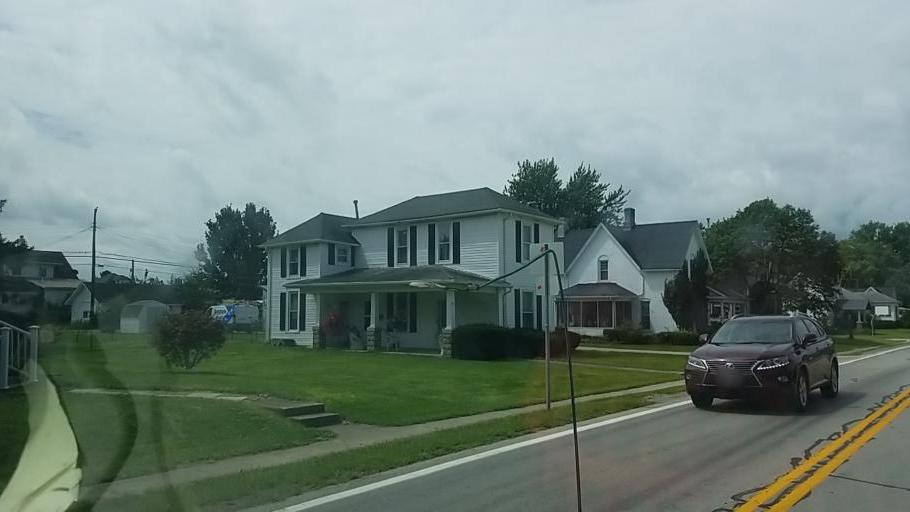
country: US
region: Ohio
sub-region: Fayette County
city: Jeffersonville
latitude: 39.6515
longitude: -83.5596
